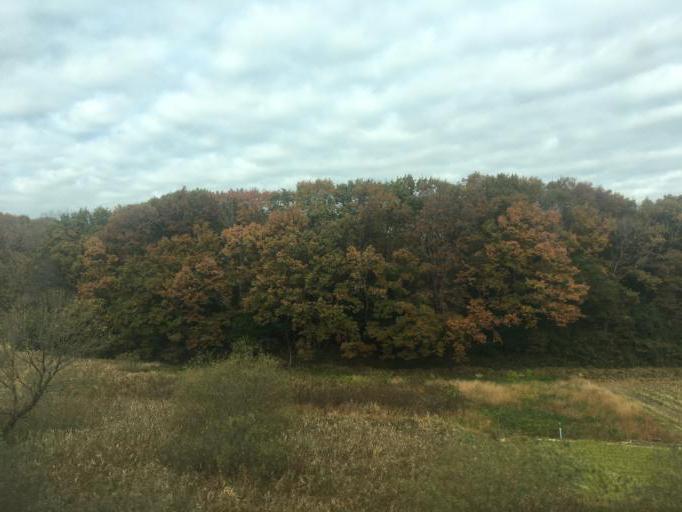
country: JP
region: Ibaraki
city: Ishioka
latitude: 36.1386
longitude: 140.2696
